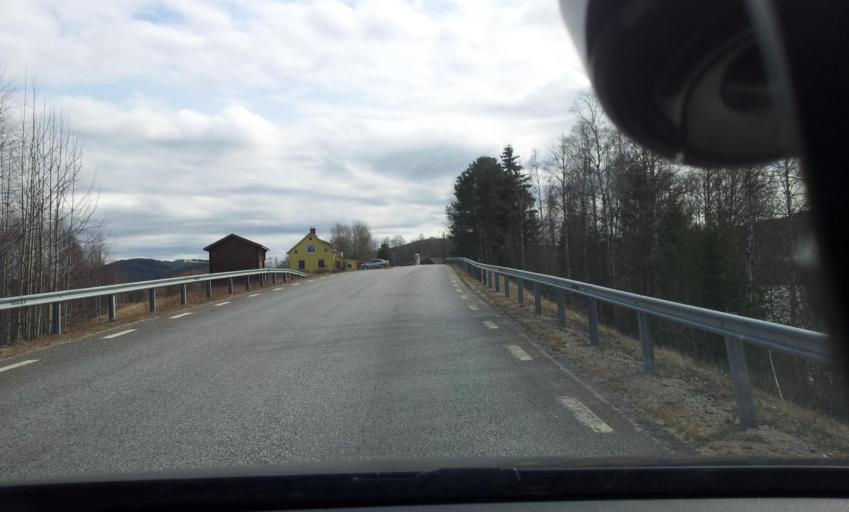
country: SE
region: Gaevleborg
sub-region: Ljusdals Kommun
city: Farila
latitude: 61.7779
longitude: 15.9479
